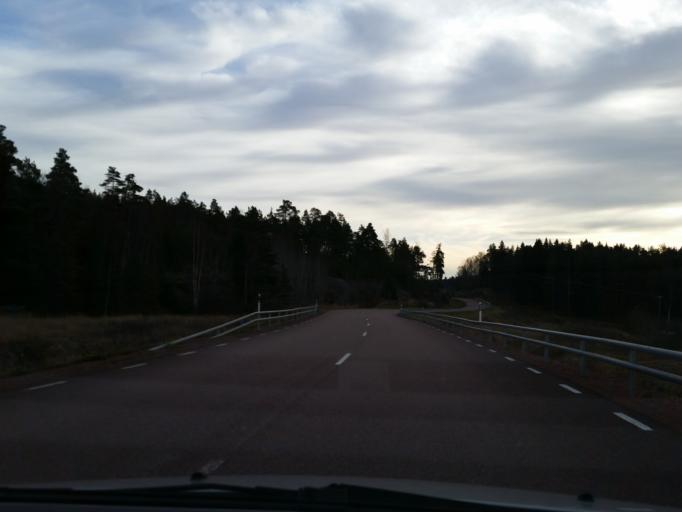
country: AX
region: Alands landsbygd
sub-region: Saltvik
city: Saltvik
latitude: 60.2510
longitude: 20.0387
